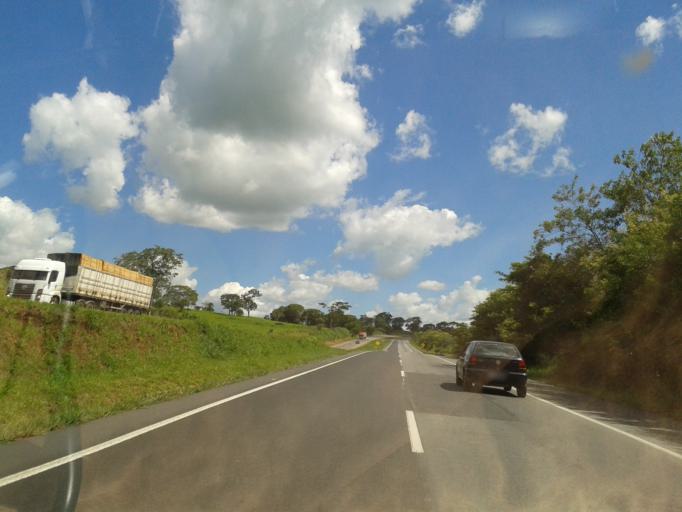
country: BR
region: Goias
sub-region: Pontalina
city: Pontalina
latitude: -17.4768
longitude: -49.2128
